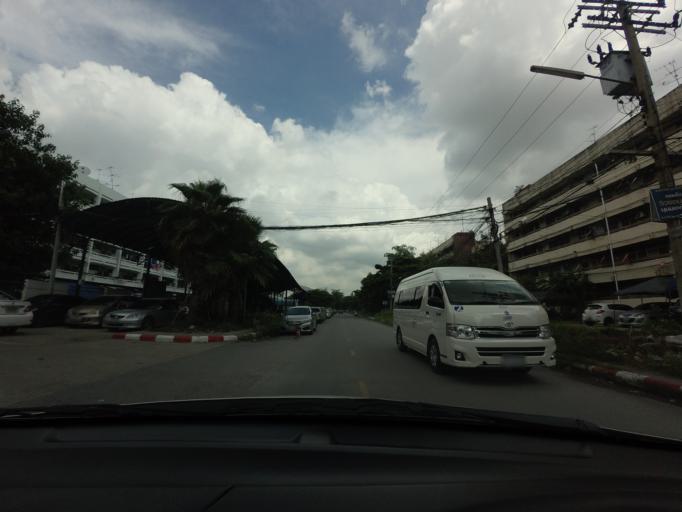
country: TH
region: Bangkok
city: Chatuchak
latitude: 13.8187
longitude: 100.5558
